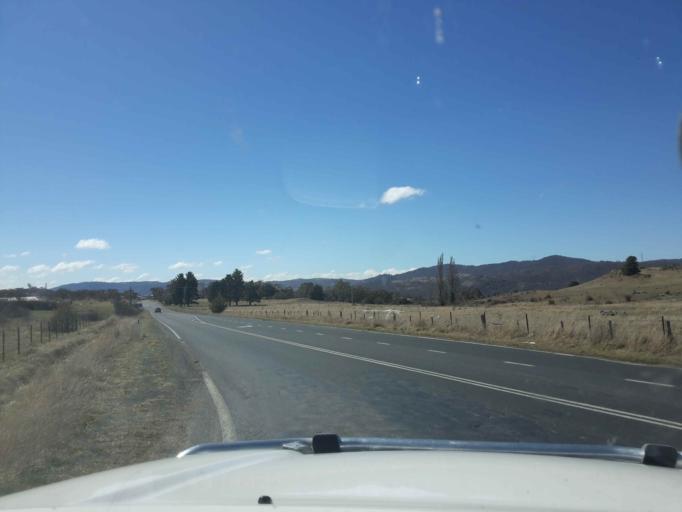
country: AU
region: New South Wales
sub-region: Snowy River
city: Jindabyne
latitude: -36.4358
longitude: 148.6070
